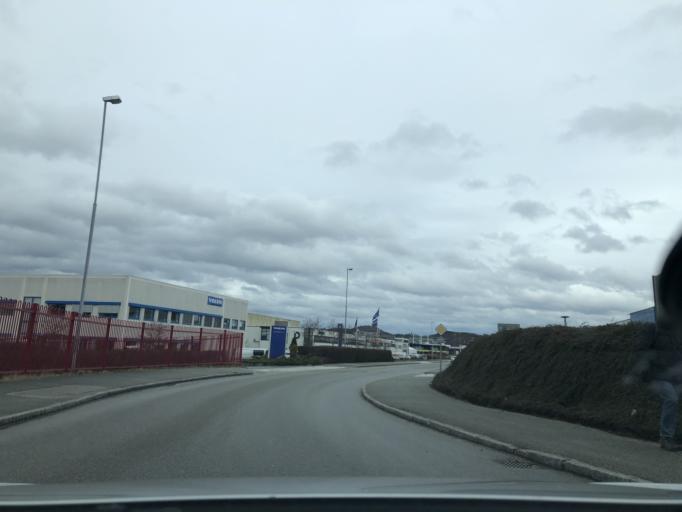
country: NO
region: Rogaland
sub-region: Sandnes
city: Sandnes
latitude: 58.8790
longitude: 5.7202
